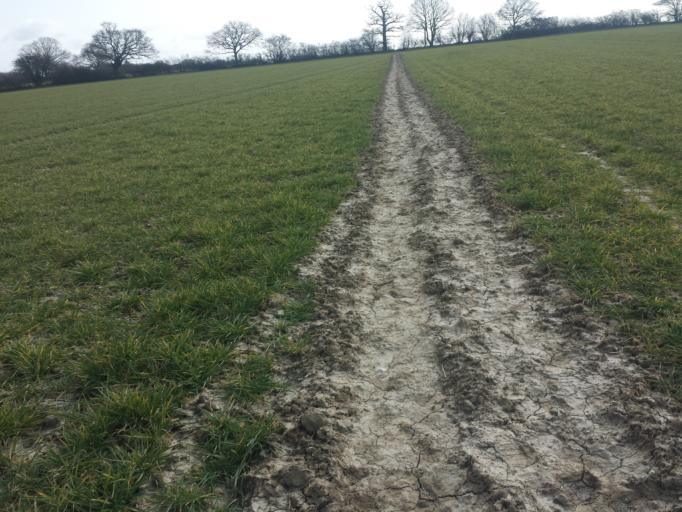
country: GB
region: England
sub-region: Essex
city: Little Clacton
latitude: 51.9042
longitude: 1.1527
